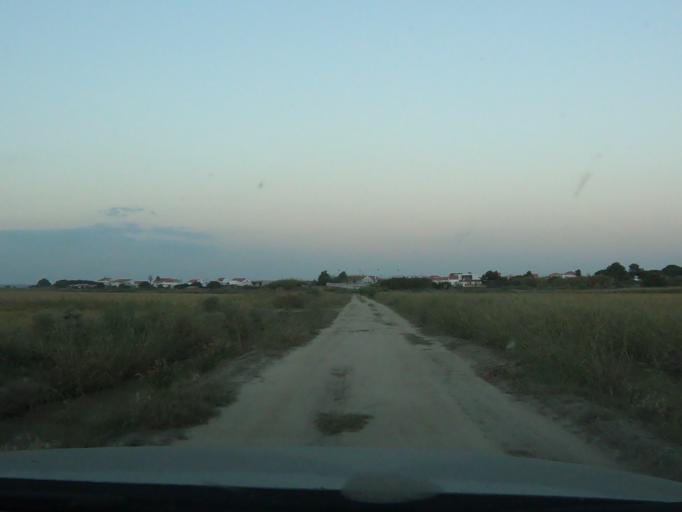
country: PT
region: Setubal
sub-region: Setubal
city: Setubal
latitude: 38.4084
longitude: -8.7581
